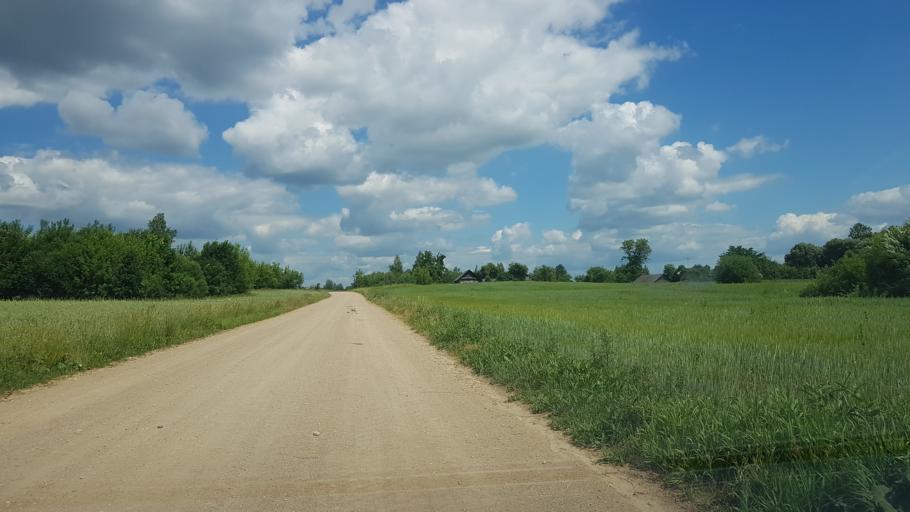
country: BY
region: Vitebsk
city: Dubrowna
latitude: 54.4893
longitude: 30.7957
